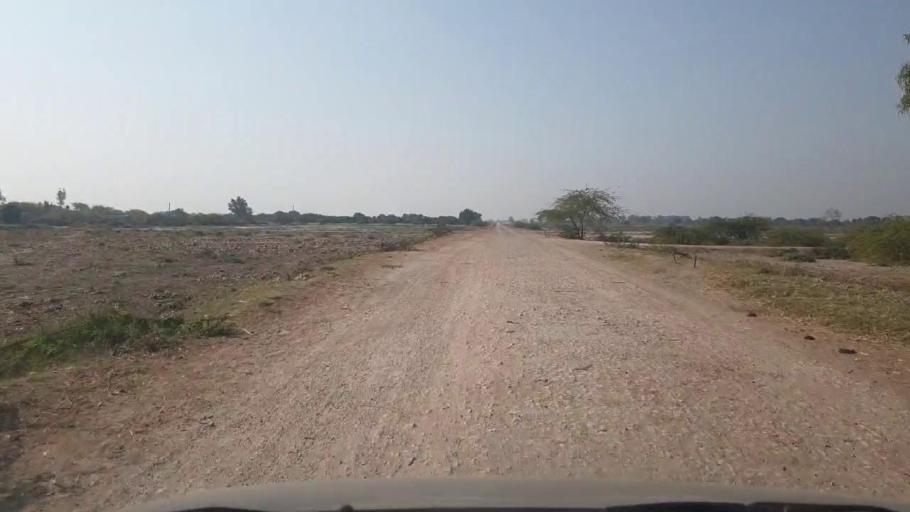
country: PK
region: Sindh
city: Mirwah Gorchani
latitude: 25.2729
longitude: 69.1191
